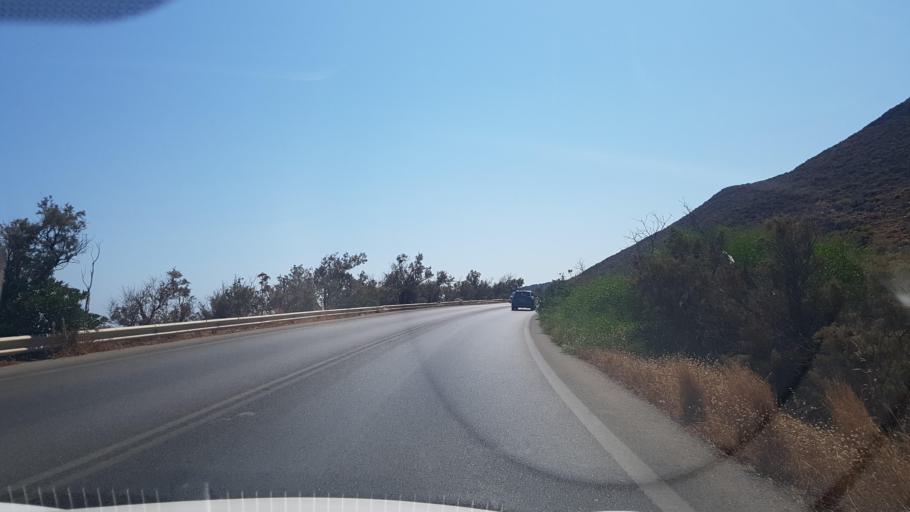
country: GR
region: Crete
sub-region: Nomos Rethymnis
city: Atsipopoulon
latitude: 35.3614
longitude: 24.3753
